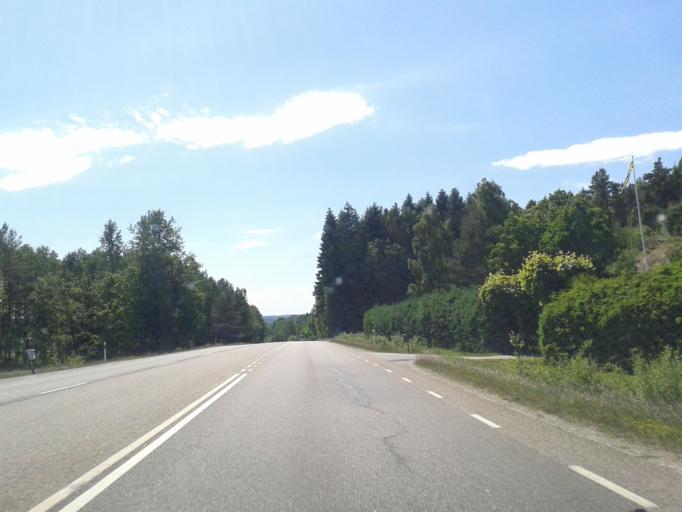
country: SE
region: Vaestra Goetaland
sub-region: Stenungsunds Kommun
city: Stora Hoga
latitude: 58.0510
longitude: 11.9026
